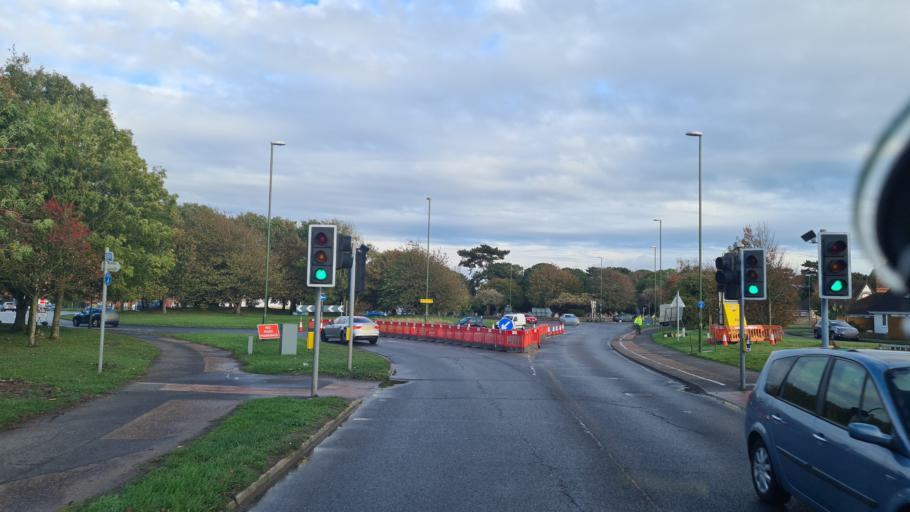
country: GB
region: England
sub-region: West Sussex
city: Littlehampton
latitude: 50.8201
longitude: -0.5299
